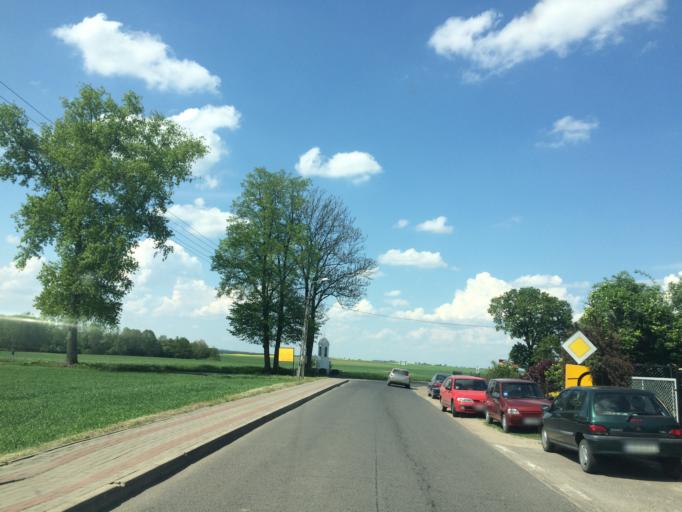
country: PL
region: Warmian-Masurian Voivodeship
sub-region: Powiat ilawski
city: Lubawa
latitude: 53.4137
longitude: 19.7543
